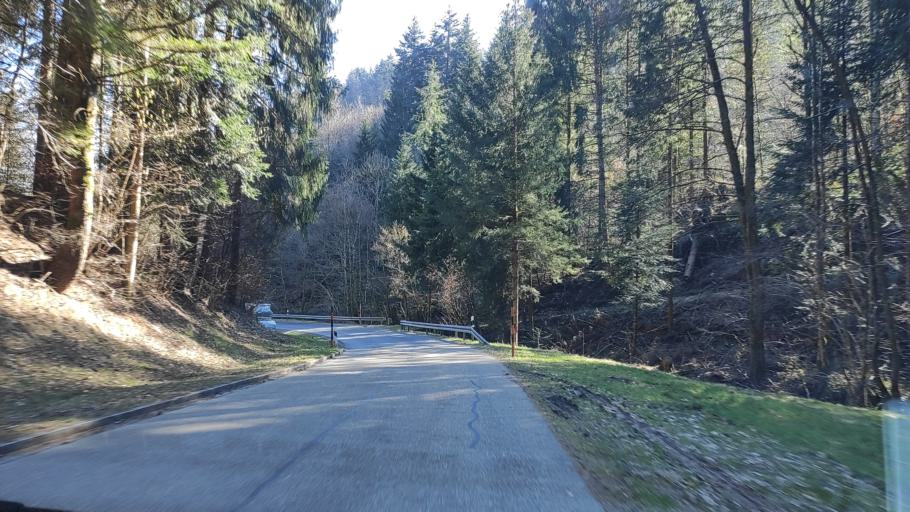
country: DE
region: Baden-Wuerttemberg
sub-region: Freiburg Region
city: Gutach im Breisgau
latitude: 48.1704
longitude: 8.0004
